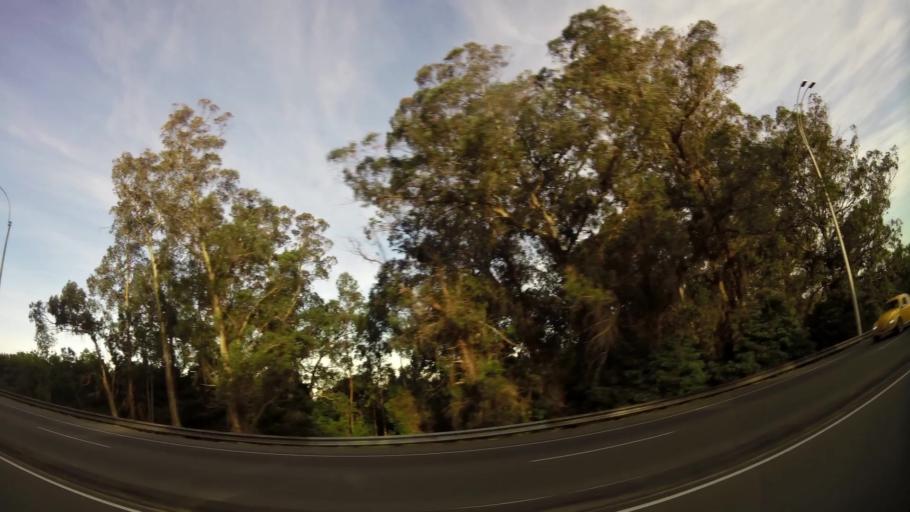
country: UY
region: Maldonado
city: Maldonado
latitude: -34.8996
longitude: -55.0373
